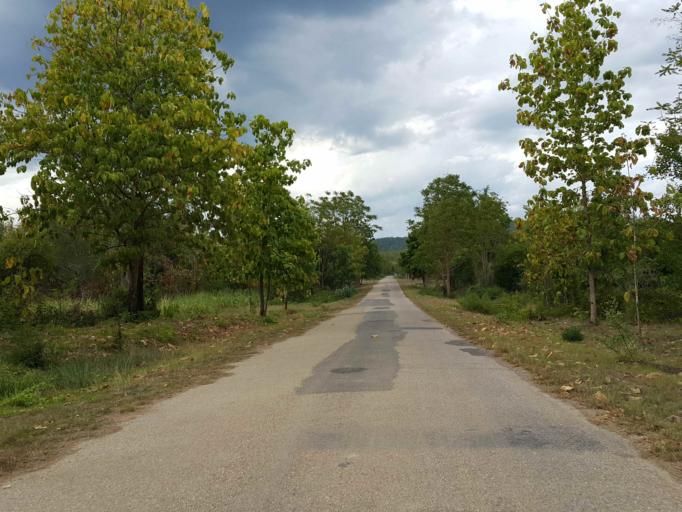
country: TH
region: Sukhothai
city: Thung Saliam
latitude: 17.3432
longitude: 99.4238
